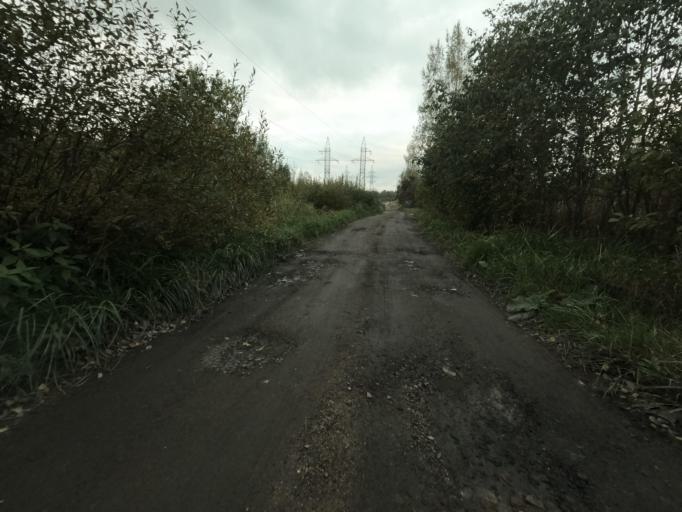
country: RU
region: St.-Petersburg
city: Sapernyy
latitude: 59.7741
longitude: 30.6511
